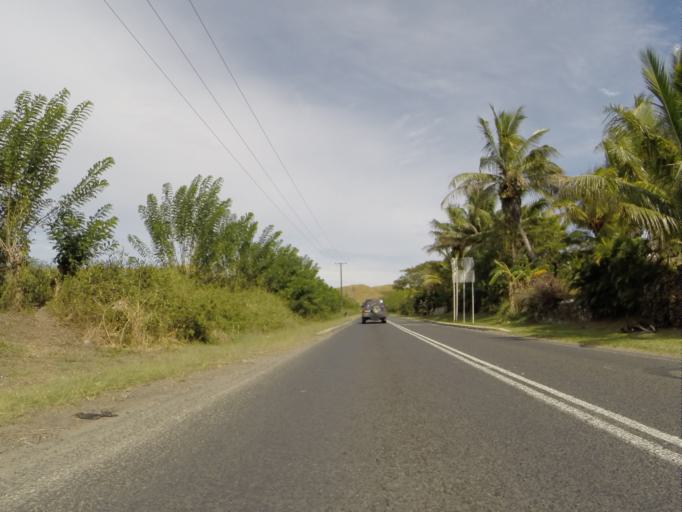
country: FJ
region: Western
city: Nadi
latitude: -18.1595
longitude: 177.4883
